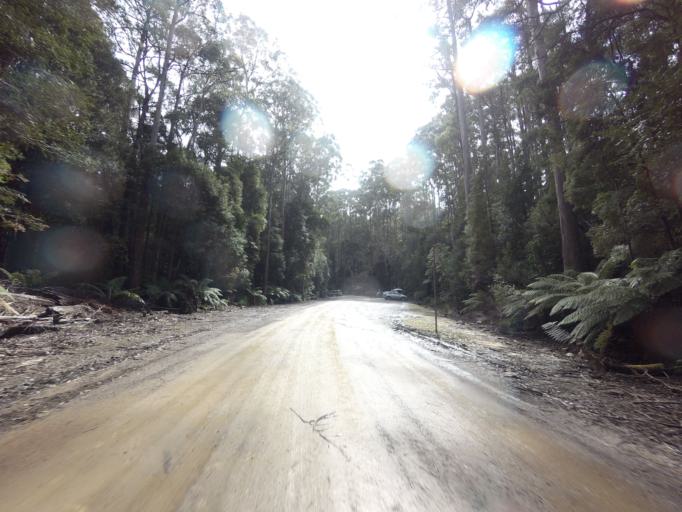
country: AU
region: Tasmania
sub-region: Huon Valley
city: Geeveston
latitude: -43.3834
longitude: 146.8419
